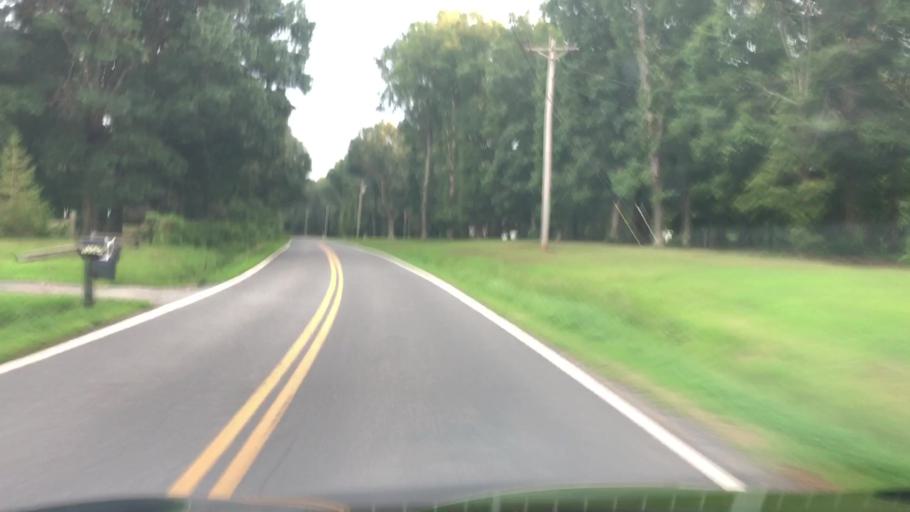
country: US
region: Virginia
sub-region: Fauquier County
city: Bealeton
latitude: 38.5459
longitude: -77.6767
